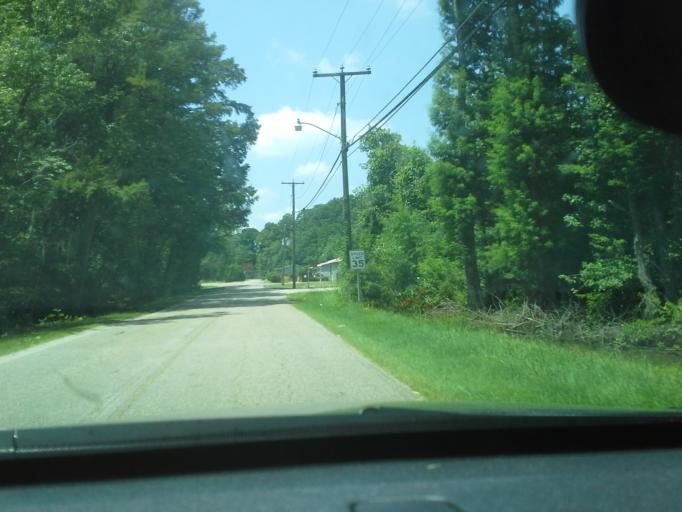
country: US
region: North Carolina
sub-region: Washington County
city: Plymouth
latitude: 35.8638
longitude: -76.7565
